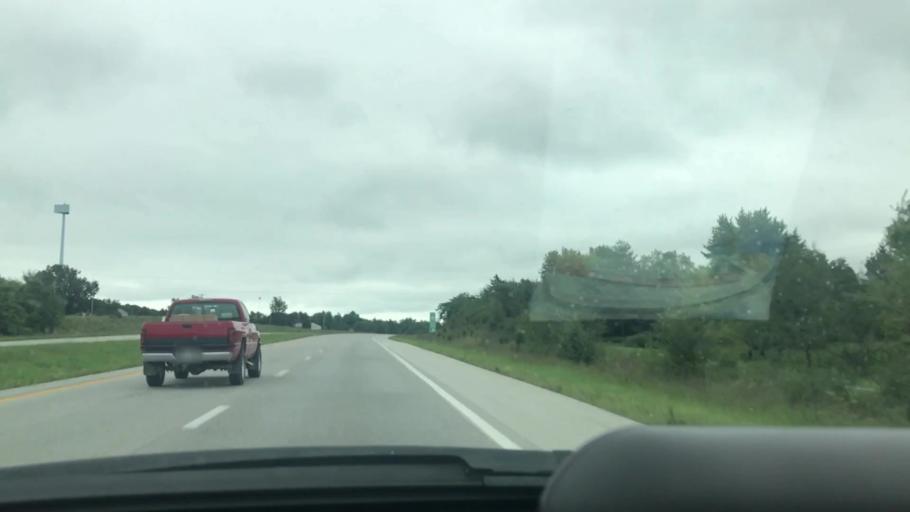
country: US
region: Missouri
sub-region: Greene County
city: Strafford
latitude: 37.2798
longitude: -93.2053
